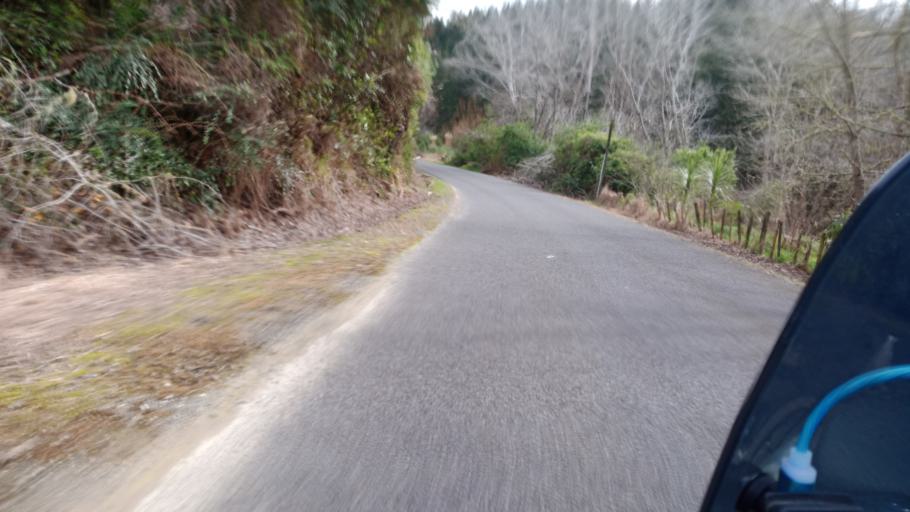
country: NZ
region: Hawke's Bay
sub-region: Wairoa District
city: Wairoa
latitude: -38.8252
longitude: 177.5111
